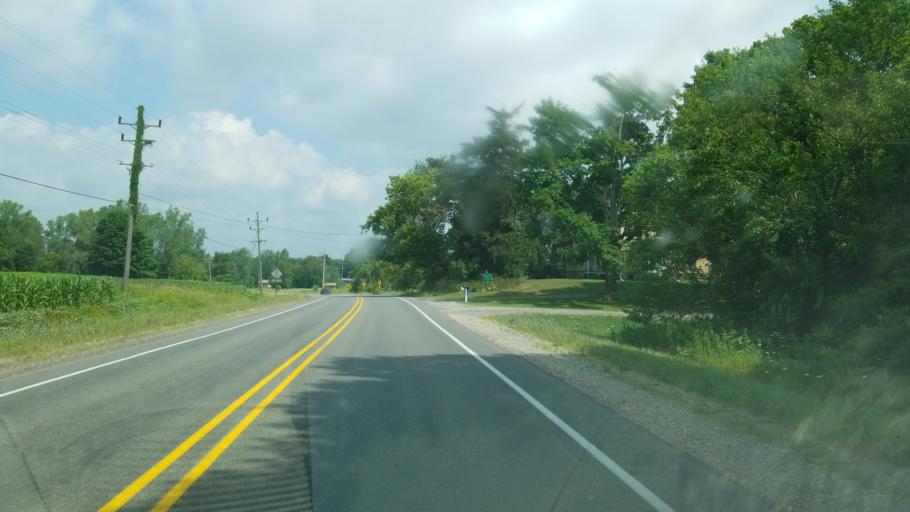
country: US
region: Michigan
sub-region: Kent County
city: Sparta
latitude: 43.1918
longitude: -85.7108
